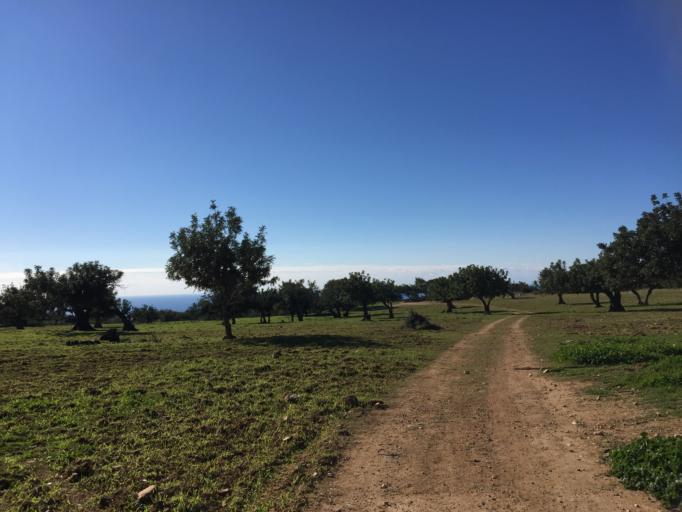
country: CY
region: Limassol
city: Pissouri
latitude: 34.6660
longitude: 32.6827
